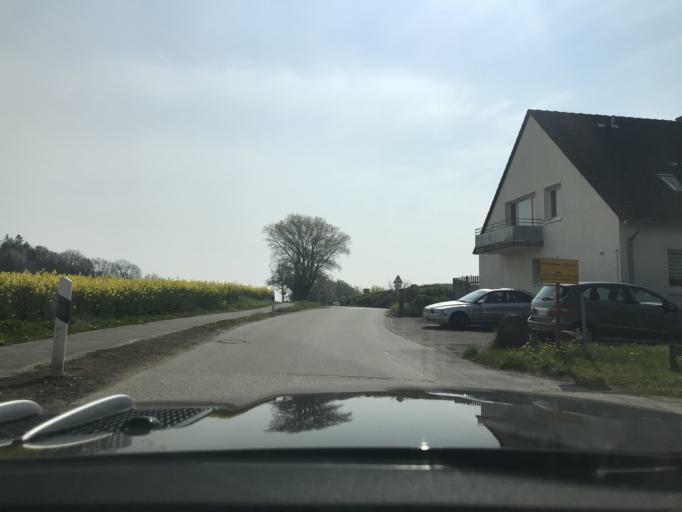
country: DE
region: Schleswig-Holstein
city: Schashagen
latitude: 54.1287
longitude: 10.9149
